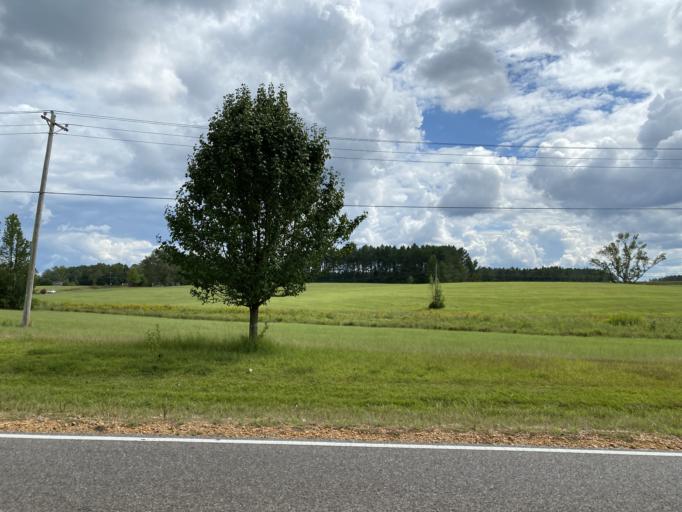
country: US
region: Mississippi
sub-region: Monroe County
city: Amory
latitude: 33.9767
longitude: -88.4223
